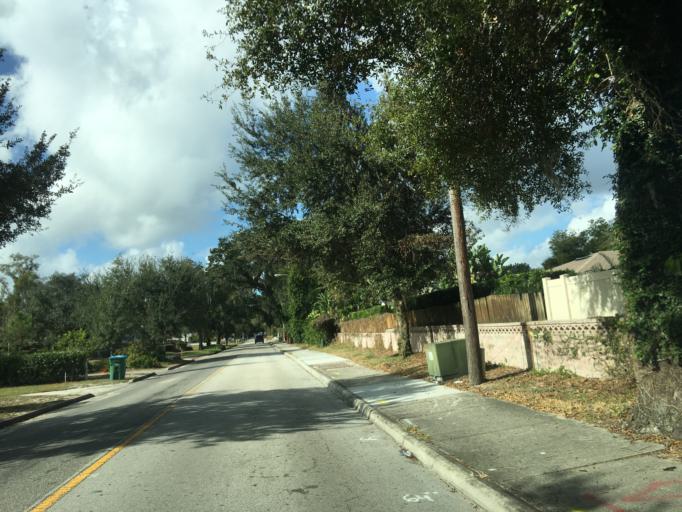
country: US
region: Florida
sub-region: Orange County
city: Maitland
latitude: 28.6102
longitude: -81.3591
